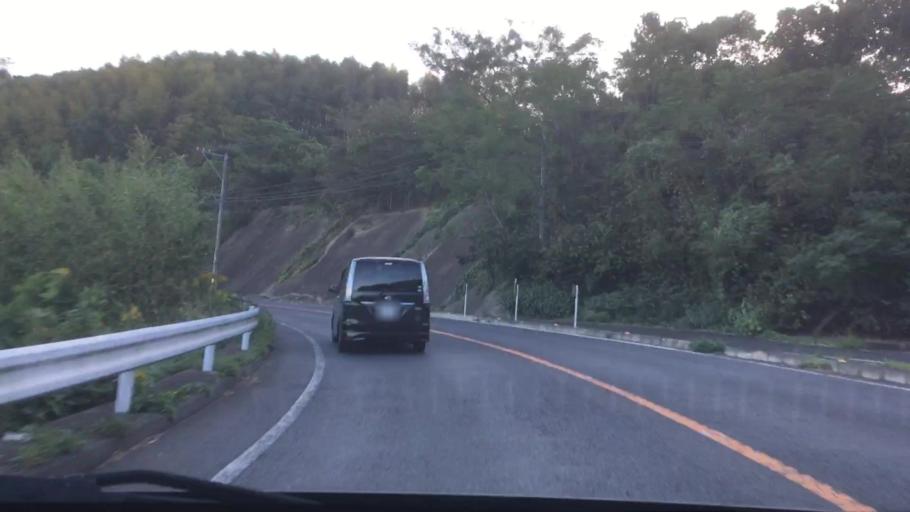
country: JP
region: Nagasaki
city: Sasebo
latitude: 33.0920
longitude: 129.7569
